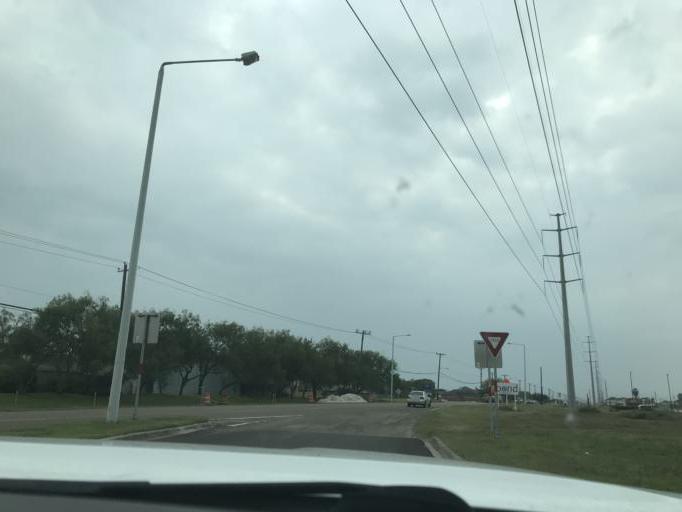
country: US
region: Texas
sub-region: Nueces County
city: Corpus Christi
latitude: 27.6706
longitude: -97.3560
